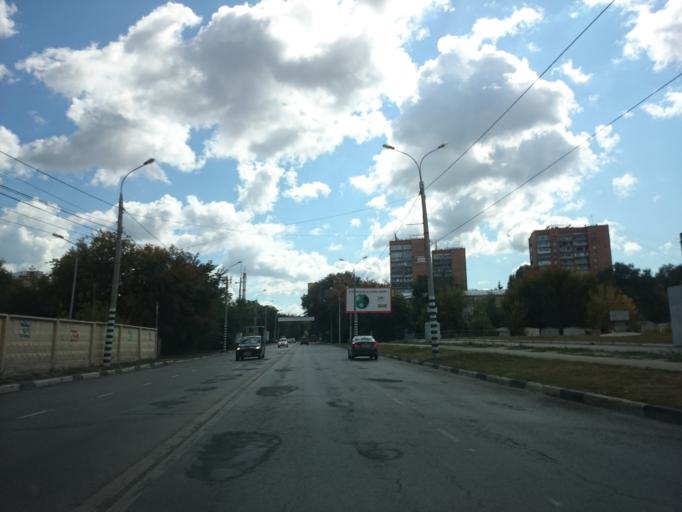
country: RU
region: Samara
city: Samara
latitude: 53.2146
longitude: 50.1394
